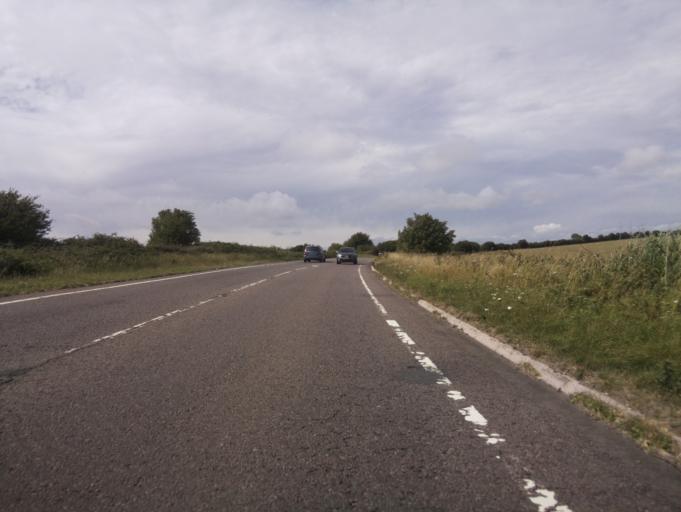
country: GB
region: England
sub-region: Dorset
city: Dorchester
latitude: 50.7718
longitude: -2.5386
